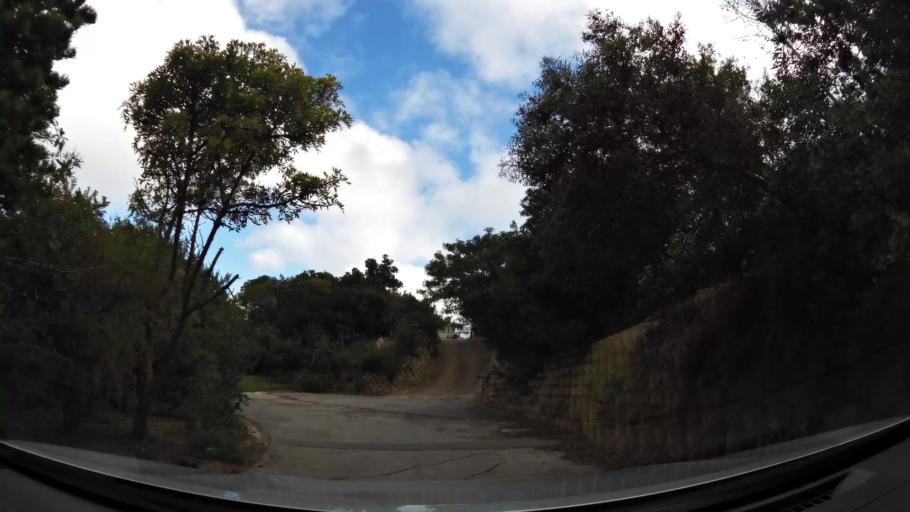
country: ZA
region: Western Cape
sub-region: Eden District Municipality
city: Plettenberg Bay
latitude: -34.0836
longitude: 23.3606
